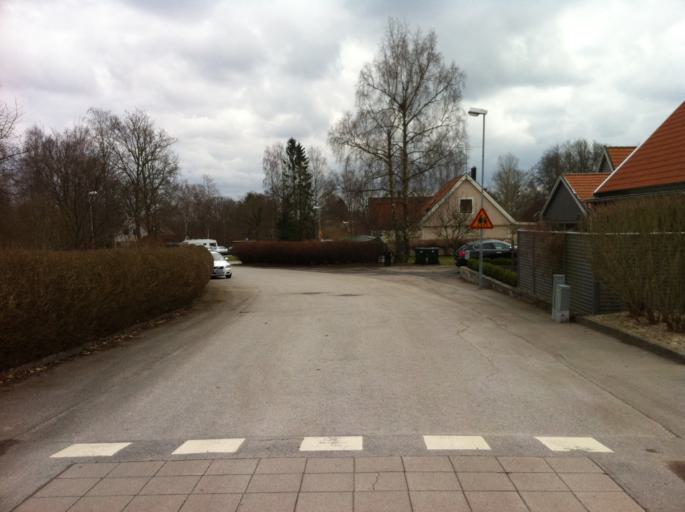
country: SE
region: Skane
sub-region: Hoors Kommun
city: Satofta
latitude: 55.9080
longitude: 13.5473
